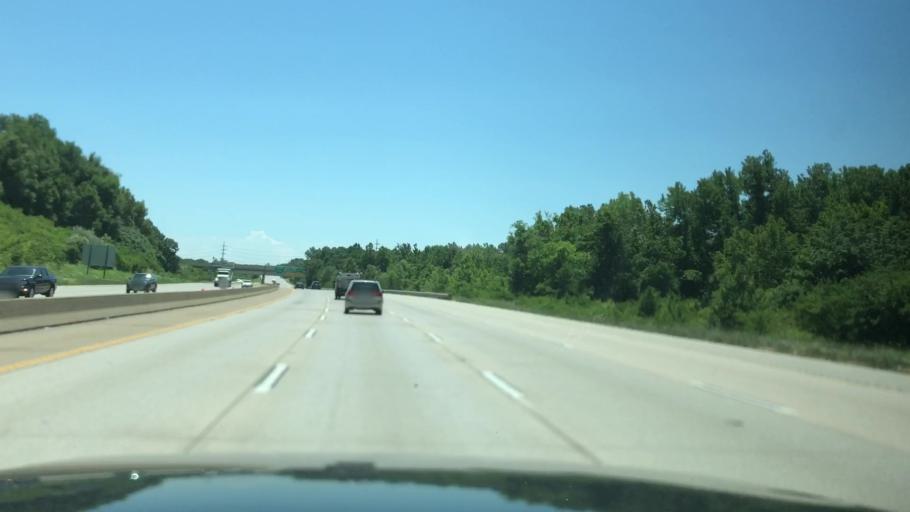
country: US
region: Missouri
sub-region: Saint Louis County
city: Bridgeton
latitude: 38.7788
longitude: -90.4156
